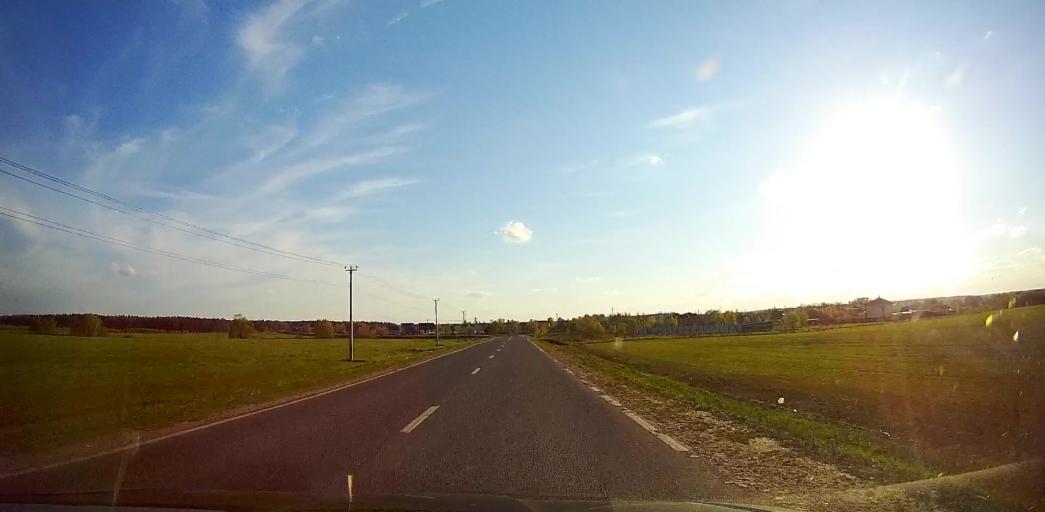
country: RU
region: Moskovskaya
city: Bronnitsy
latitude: 55.2837
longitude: 38.1769
